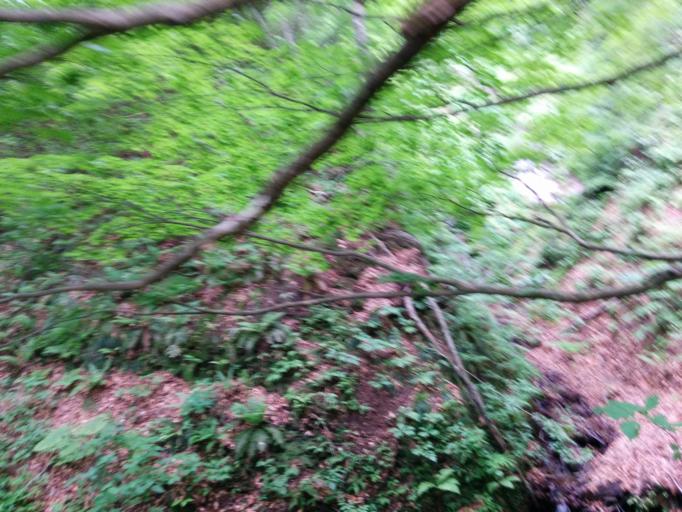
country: JP
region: Aomori
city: Hirosaki
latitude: 40.5214
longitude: 140.1733
